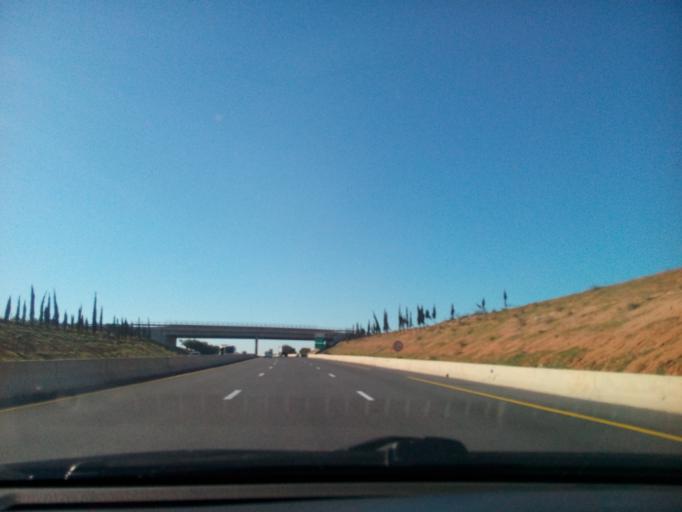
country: DZ
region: Relizane
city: Djidiouia
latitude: 35.8981
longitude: 0.7125
